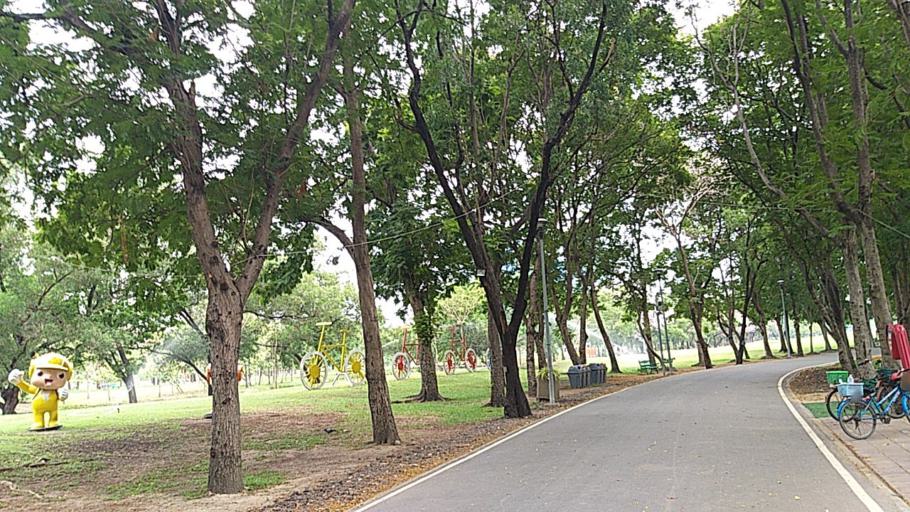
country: TH
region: Bangkok
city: Chatuchak
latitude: 13.8155
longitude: 100.5536
